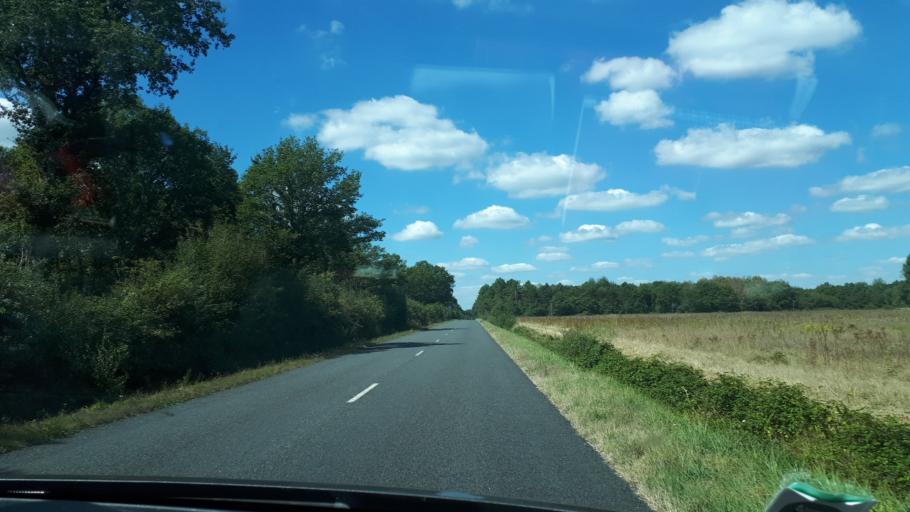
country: FR
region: Centre
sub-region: Departement du Loir-et-Cher
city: Dhuizon
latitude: 47.5345
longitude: 1.7039
